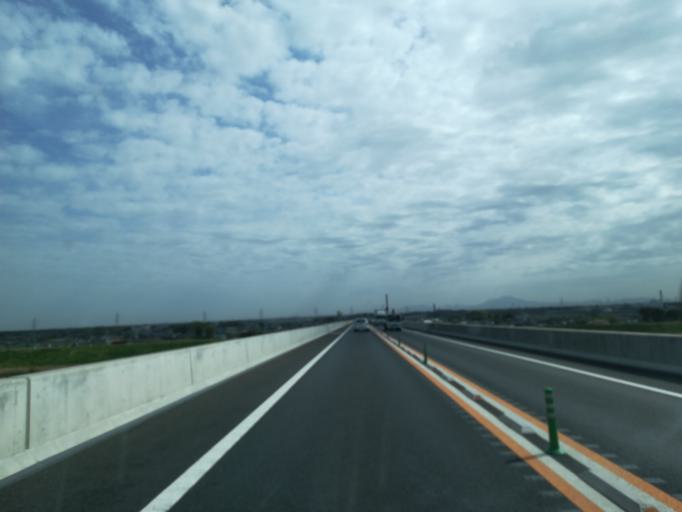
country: JP
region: Ibaraki
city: Sakai
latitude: 36.1169
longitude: 139.7677
